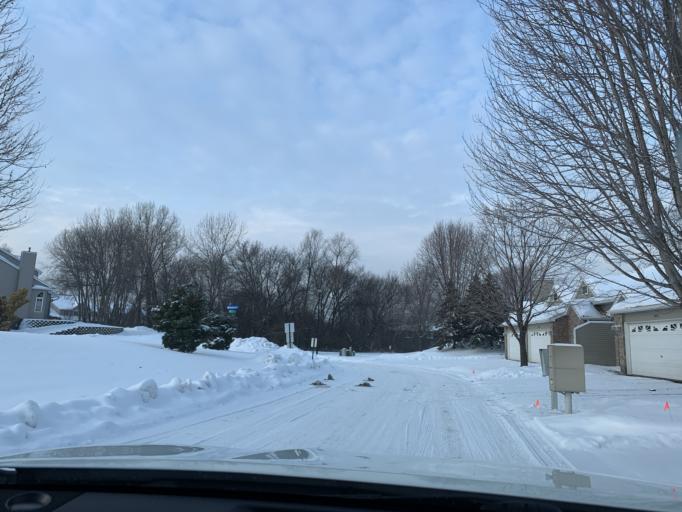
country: US
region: Minnesota
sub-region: Anoka County
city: Coon Rapids
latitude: 45.1646
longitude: -93.2902
